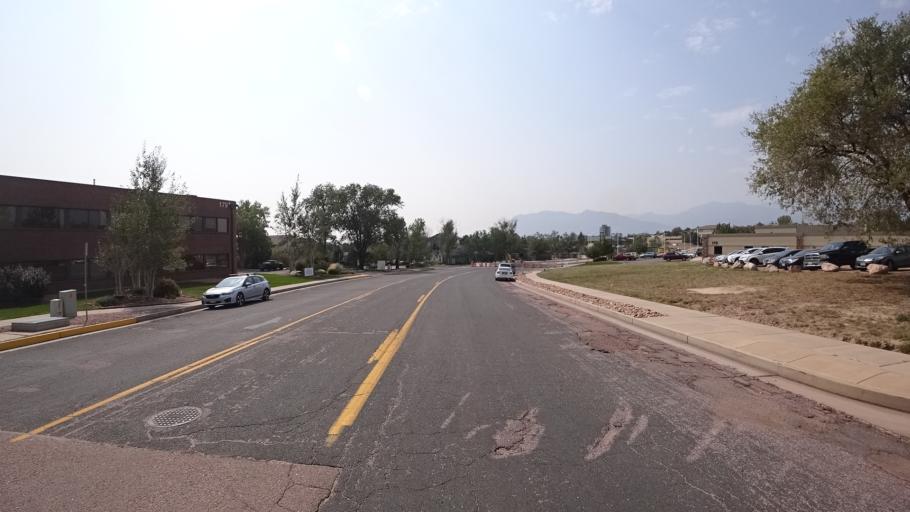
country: US
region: Colorado
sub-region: El Paso County
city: Colorado Springs
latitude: 38.8298
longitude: -104.7857
